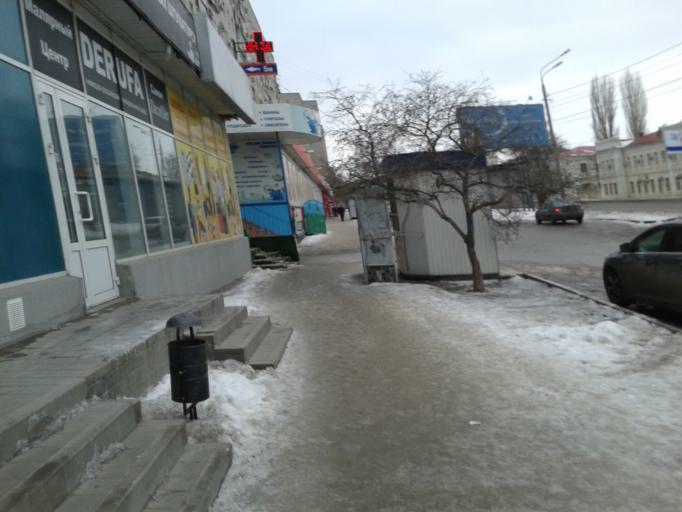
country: RU
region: Volgograd
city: Volgograd
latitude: 48.7267
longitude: 44.5187
